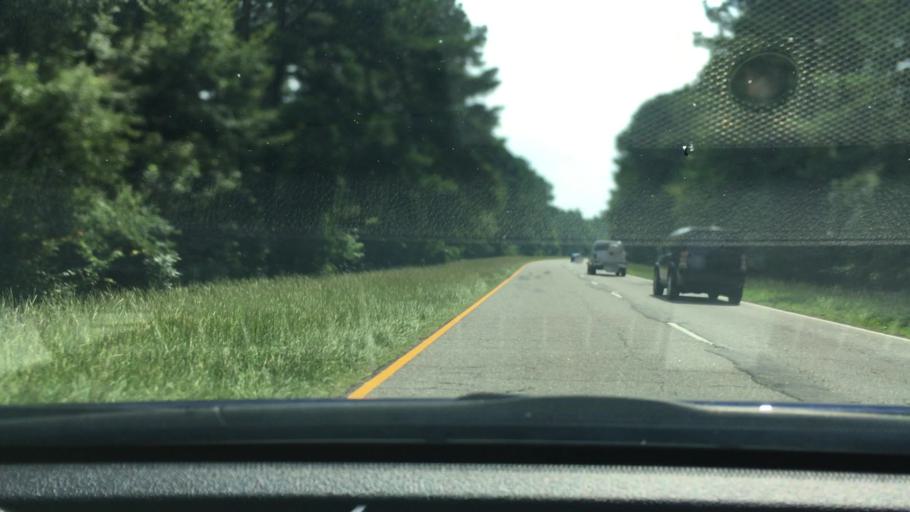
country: US
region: South Carolina
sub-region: Sumter County
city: Stateburg
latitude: 33.9525
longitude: -80.5693
